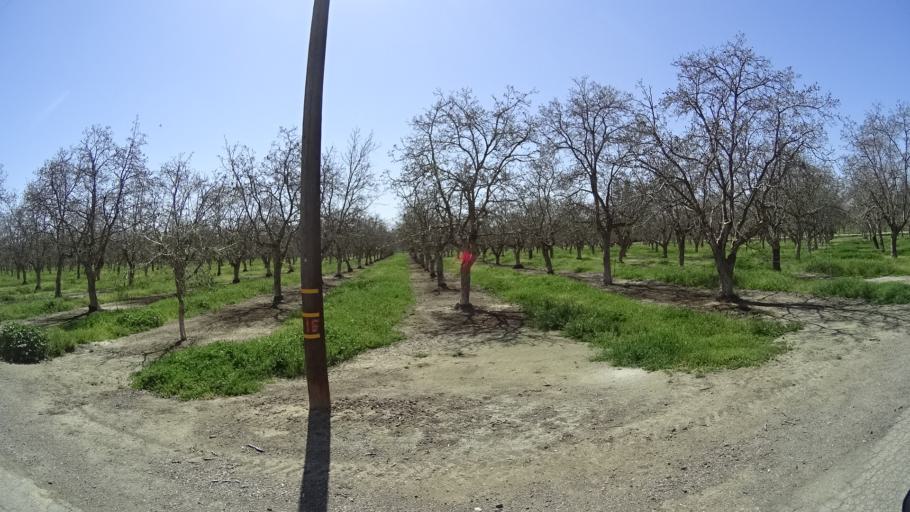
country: US
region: California
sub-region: Glenn County
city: Willows
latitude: 39.4436
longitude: -121.9854
